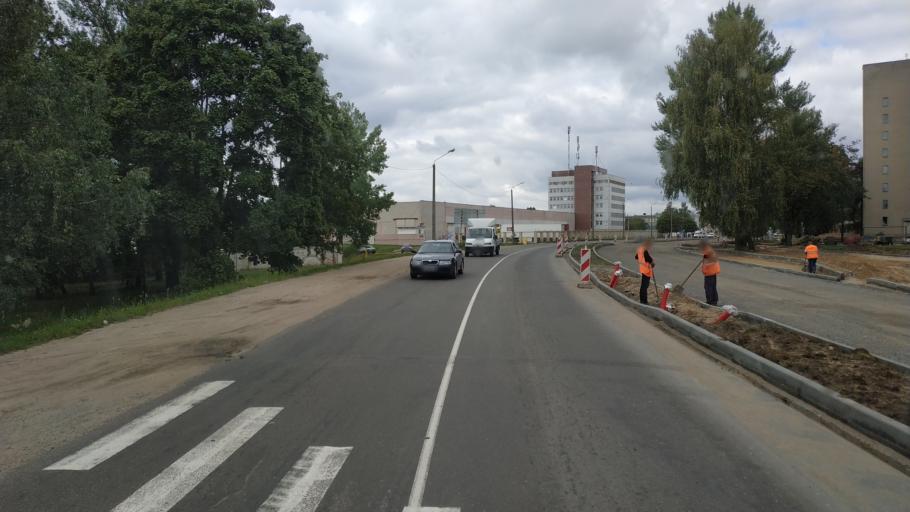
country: BY
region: Mogilev
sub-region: Mahilyowski Rayon
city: Veyno
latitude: 53.8801
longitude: 30.4094
